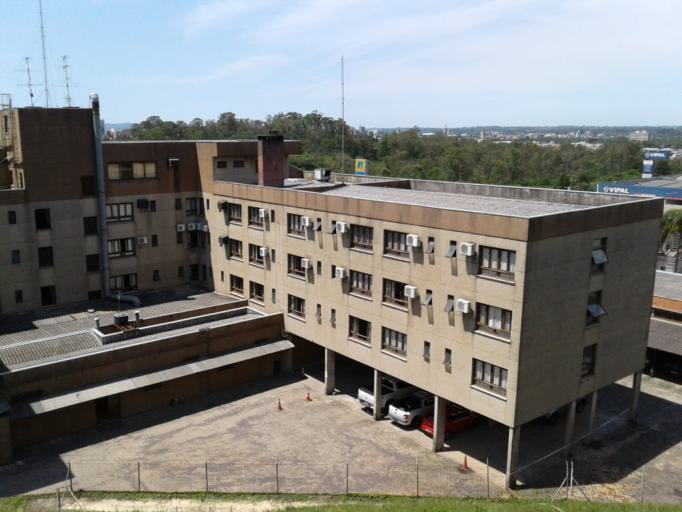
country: BR
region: Rio Grande do Sul
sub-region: Gravatai
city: Gravatai
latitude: -29.9484
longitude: -51.0114
